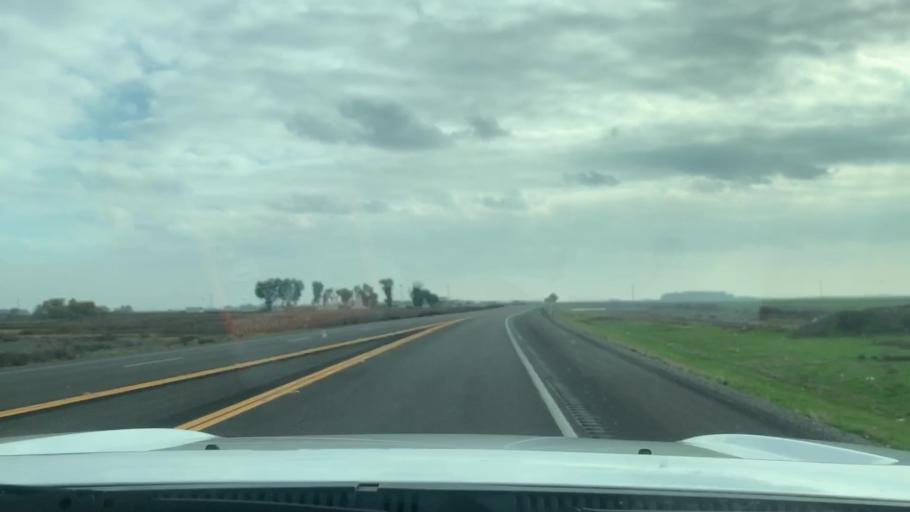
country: US
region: California
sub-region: Kings County
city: Lemoore
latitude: 36.2731
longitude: -119.8079
